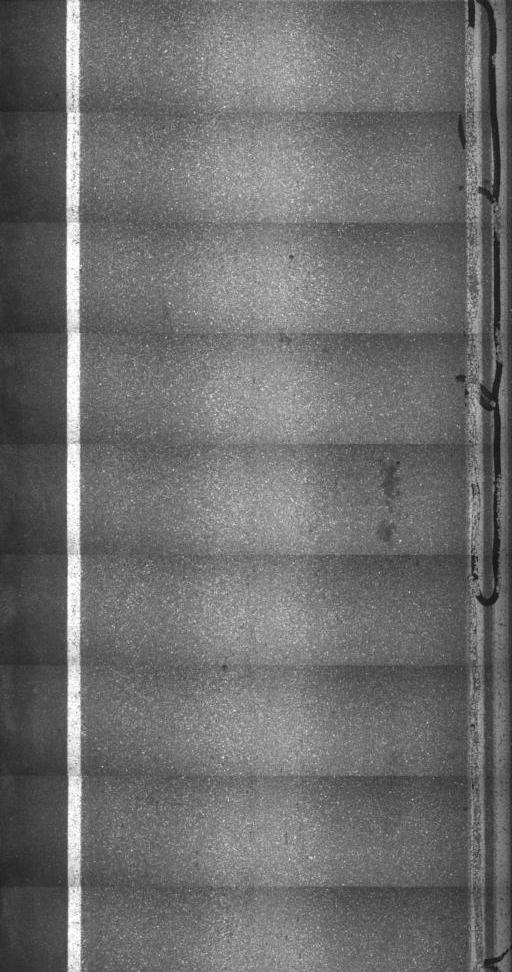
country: US
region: Vermont
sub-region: Windham County
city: Newfane
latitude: 42.9921
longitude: -72.6519
